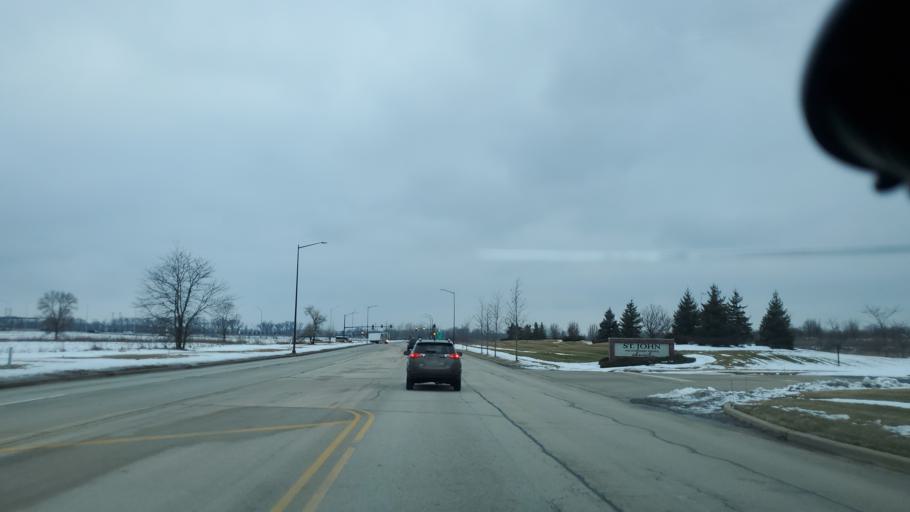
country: US
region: Illinois
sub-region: DuPage County
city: Warrenville
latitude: 41.8074
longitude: -88.2431
